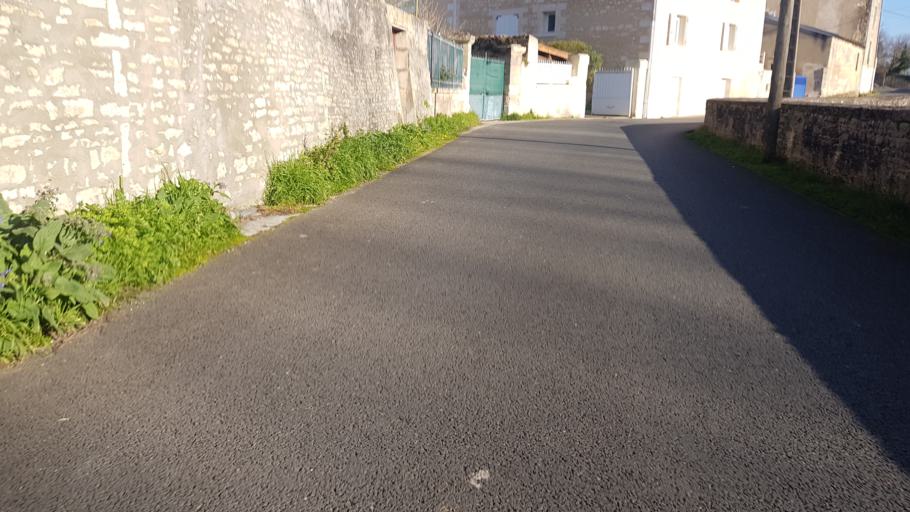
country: FR
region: Poitou-Charentes
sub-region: Departement de la Vienne
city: Chasseneuil-du-Poitou
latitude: 46.6406
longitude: 0.3506
